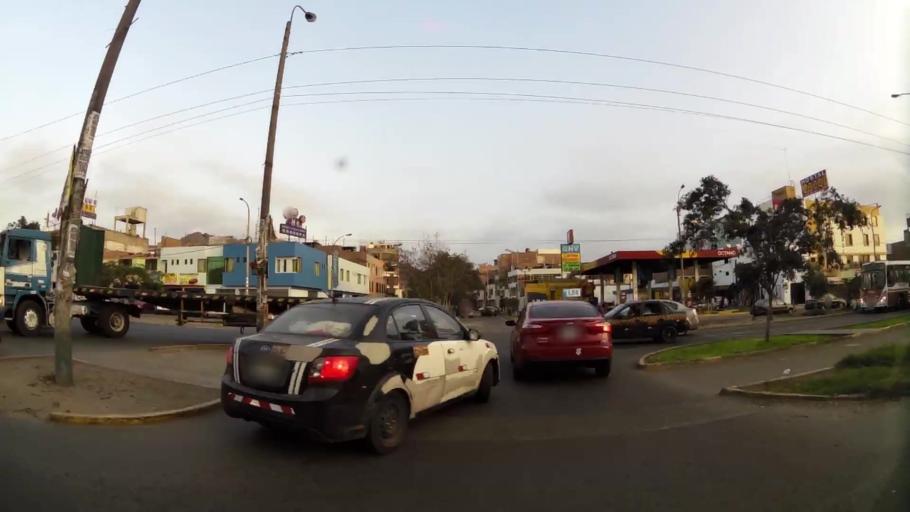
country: PE
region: Lima
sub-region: Lima
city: Independencia
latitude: -12.0118
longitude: -77.0748
